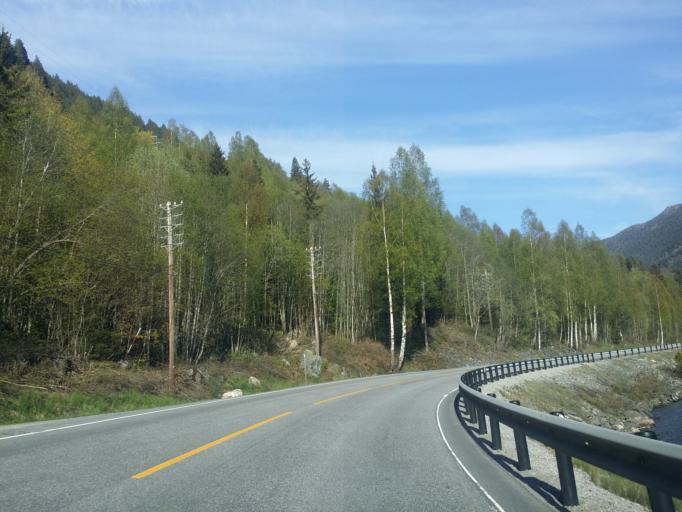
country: NO
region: Telemark
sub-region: Seljord
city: Seljord
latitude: 59.6101
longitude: 8.7526
